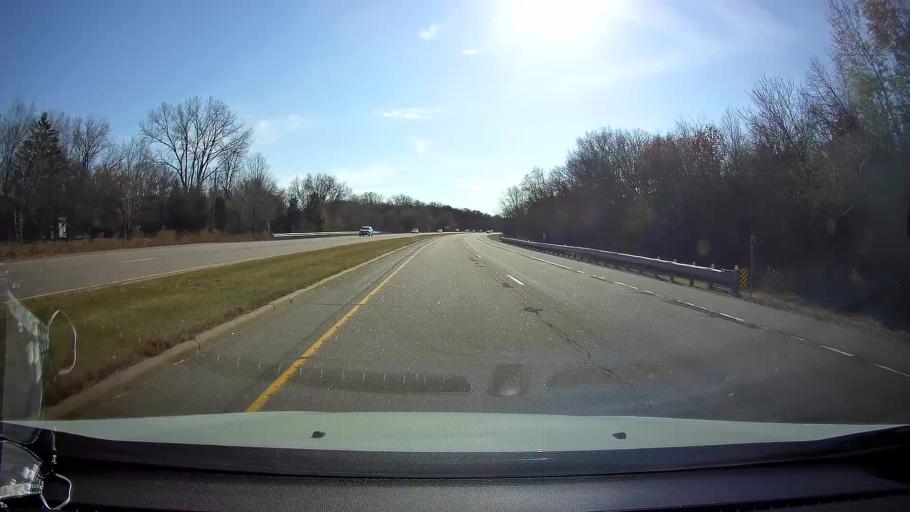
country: US
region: Minnesota
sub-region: Ramsey County
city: Arden Hills
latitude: 45.0430
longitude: -93.1572
